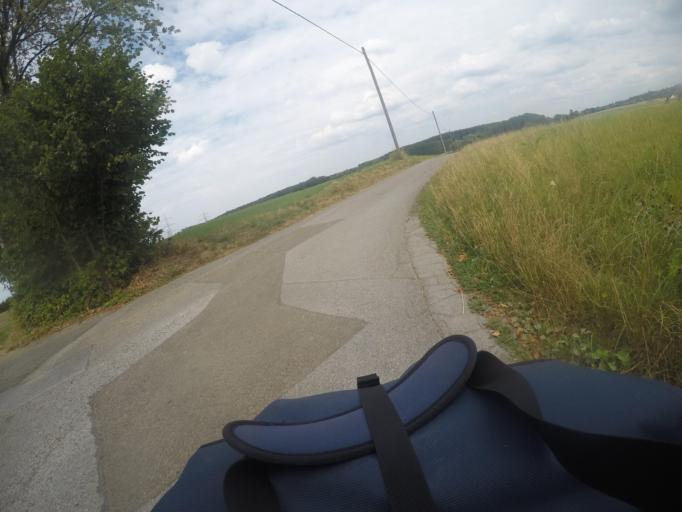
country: DE
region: North Rhine-Westphalia
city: Haan
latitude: 51.2160
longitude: 7.0250
